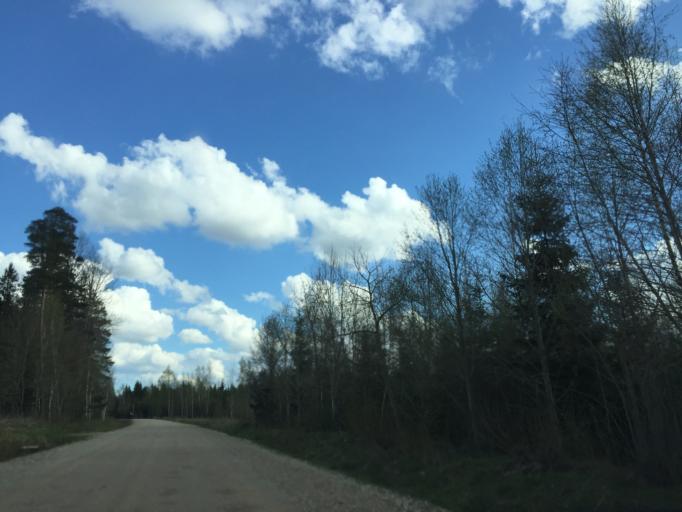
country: LV
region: Beverina
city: Murmuiza
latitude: 57.4647
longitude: 25.5016
